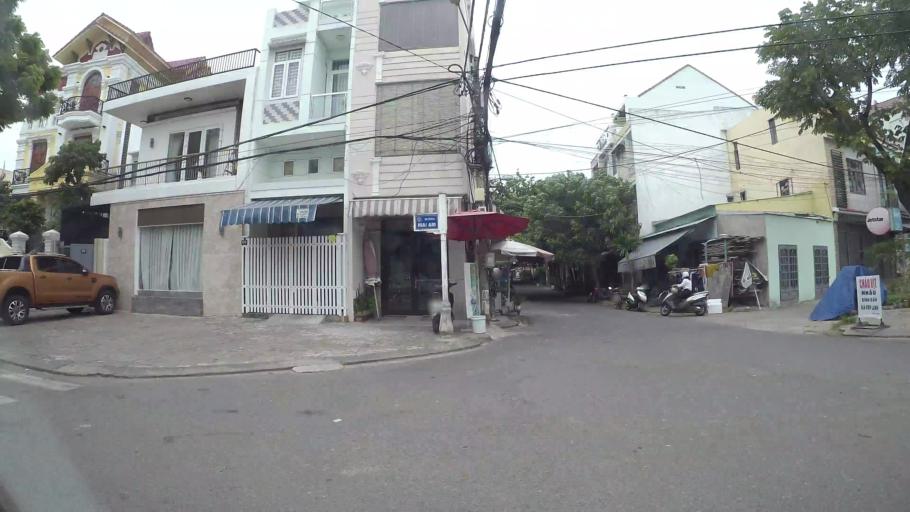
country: VN
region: Da Nang
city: Da Nang
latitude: 16.0862
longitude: 108.2165
